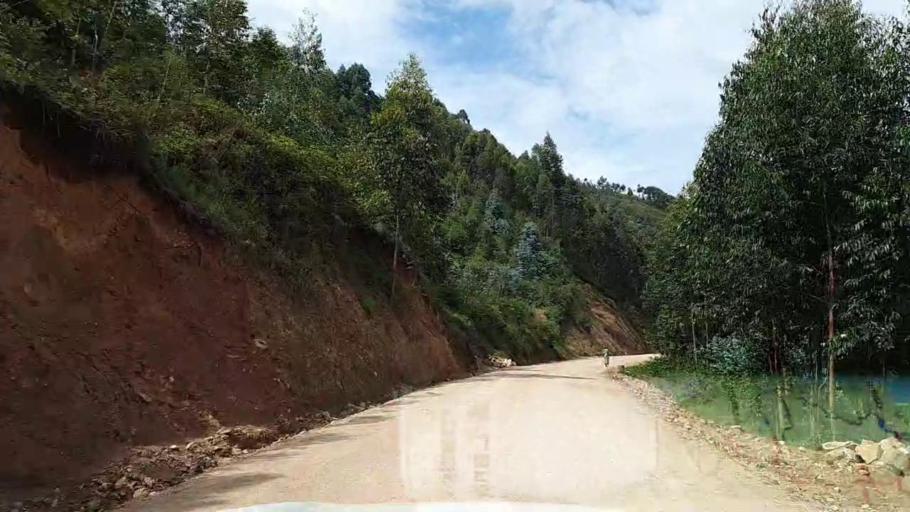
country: RW
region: Southern Province
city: Nzega
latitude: -2.3364
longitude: 29.4412
